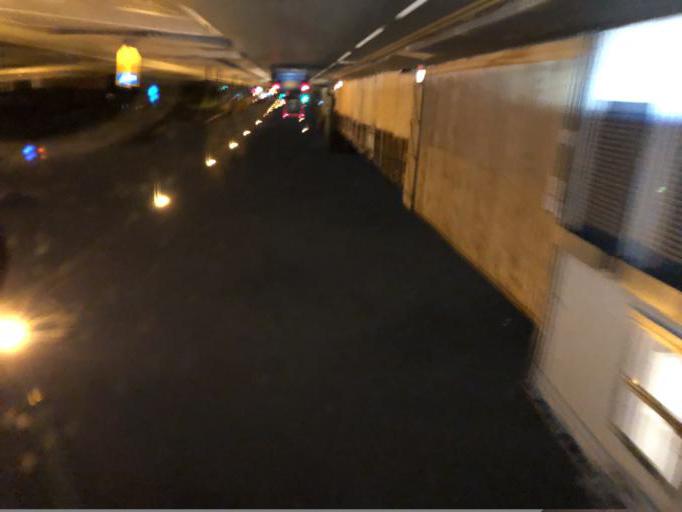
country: GB
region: England
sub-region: Manchester
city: Failsworth
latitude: 53.5122
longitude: -2.1548
